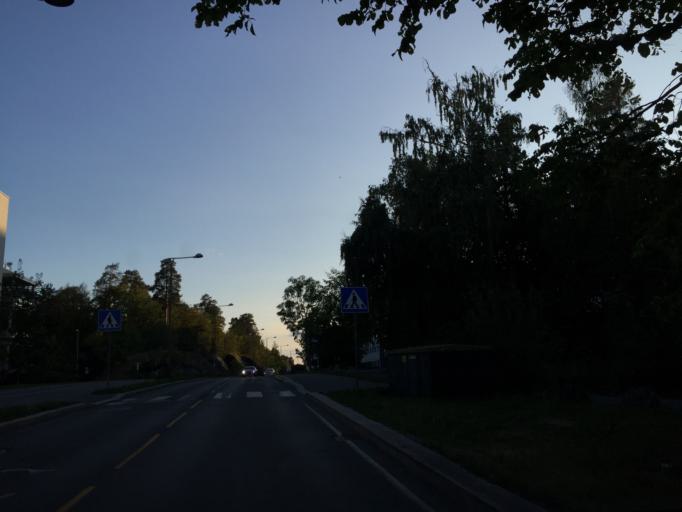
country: NO
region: Akershus
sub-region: Baerum
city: Lysaker
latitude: 59.8921
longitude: 10.6282
